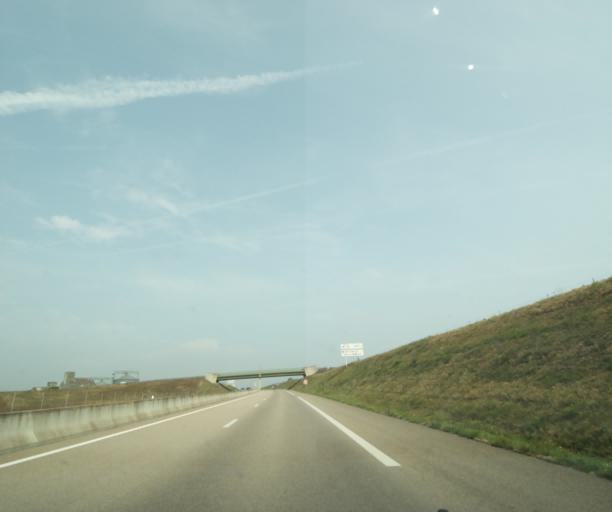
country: FR
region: Lower Normandy
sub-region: Departement de l'Orne
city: Courteilles
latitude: 48.8104
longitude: -0.1263
